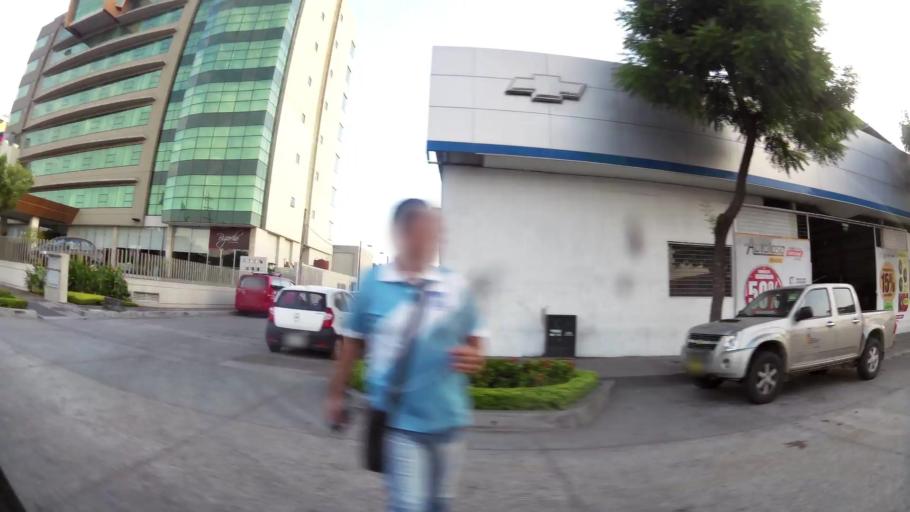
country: EC
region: Guayas
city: Eloy Alfaro
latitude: -2.1447
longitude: -79.8837
